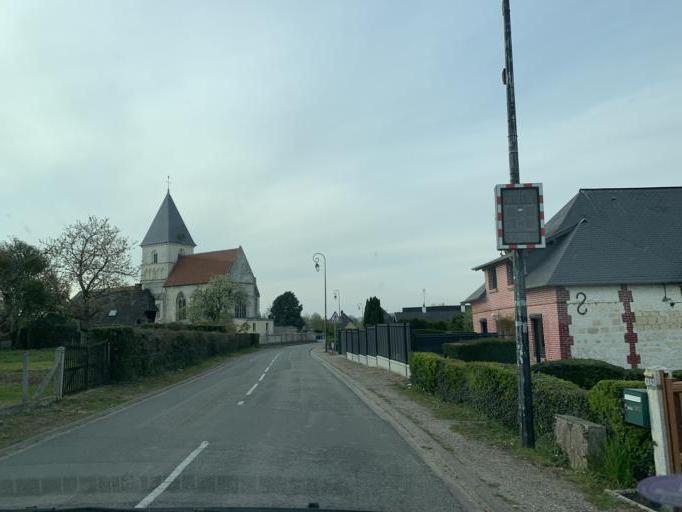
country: FR
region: Haute-Normandie
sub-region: Departement de la Seine-Maritime
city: La Mailleraye-sur-Seine
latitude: 49.4923
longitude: 0.7653
